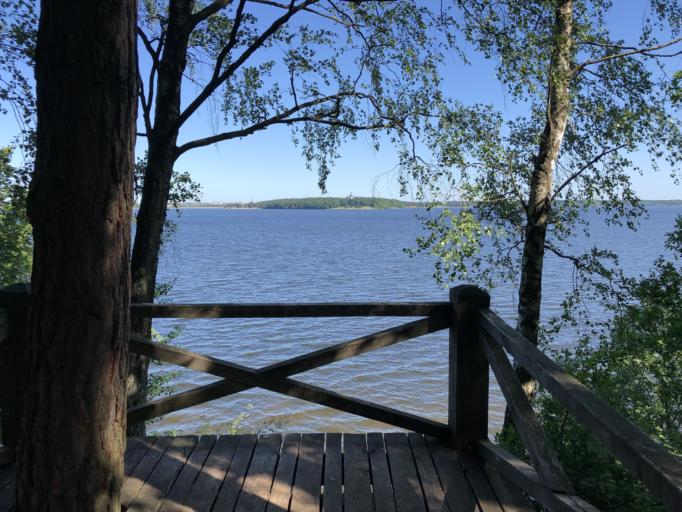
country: LT
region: Kauno apskritis
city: Dainava (Kaunas)
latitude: 54.8566
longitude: 24.0338
